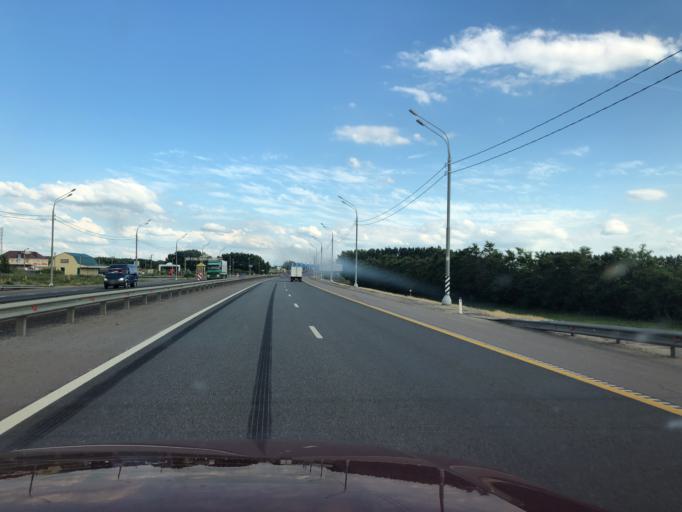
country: RU
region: Lipetsk
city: Zadonsk
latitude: 52.4347
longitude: 38.8179
